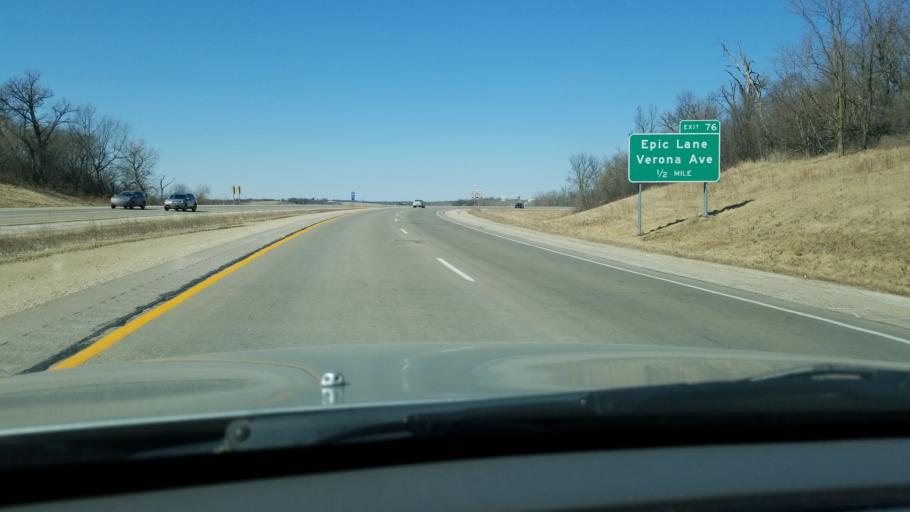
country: US
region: Wisconsin
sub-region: Dane County
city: Verona
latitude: 42.9763
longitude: -89.5540
